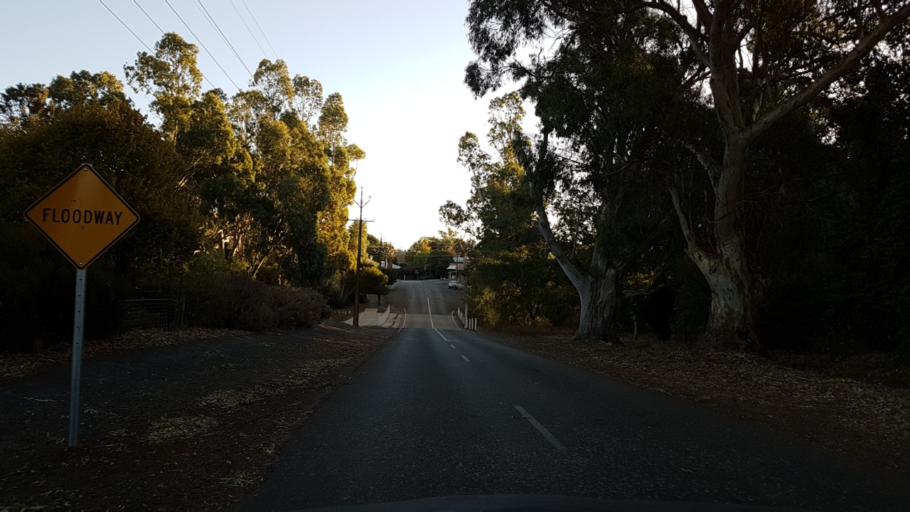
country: AU
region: South Australia
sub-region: Clare and Gilbert Valleys
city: Clare
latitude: -34.0247
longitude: 138.6875
